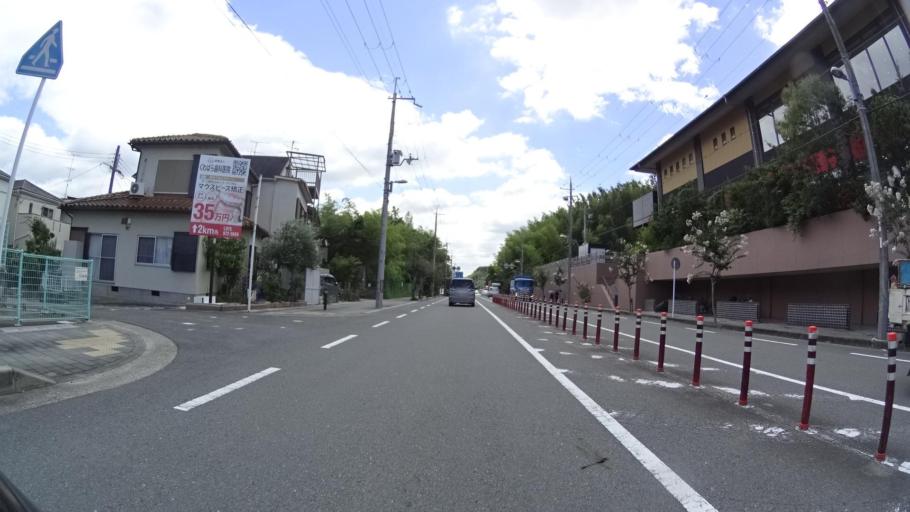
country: JP
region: Kyoto
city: Yawata
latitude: 34.8550
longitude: 135.7001
